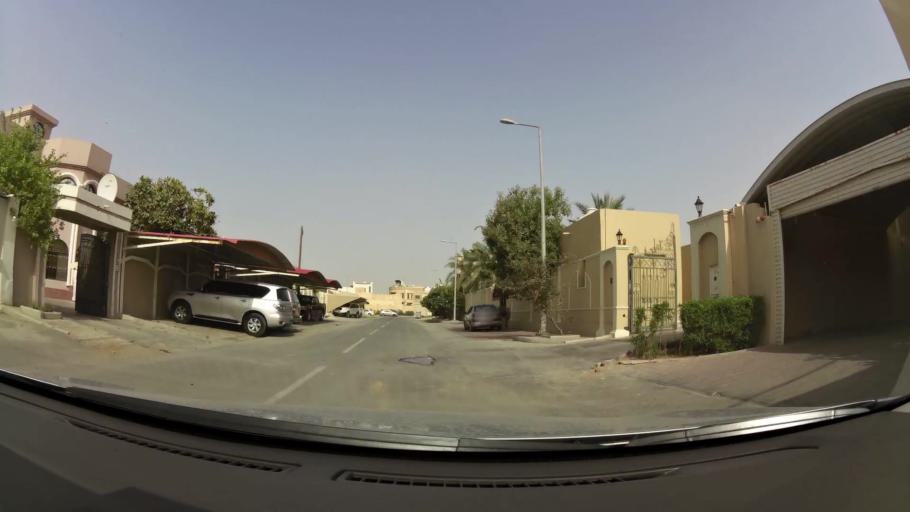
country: QA
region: Baladiyat ar Rayyan
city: Ar Rayyan
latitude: 25.2470
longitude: 51.4420
